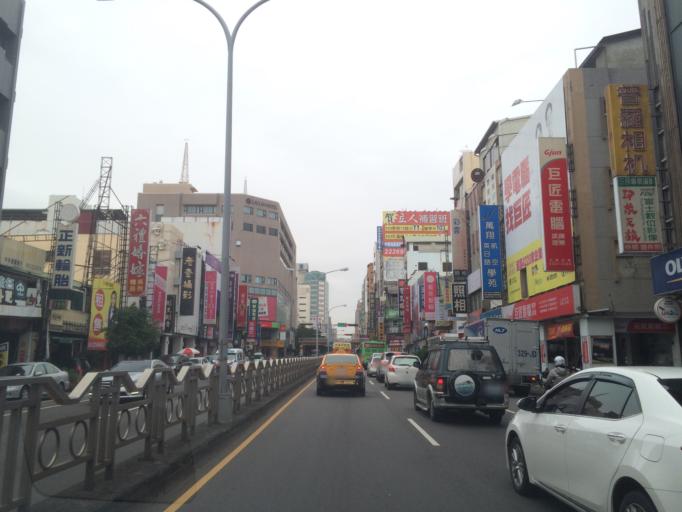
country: TW
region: Taiwan
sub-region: Taichung City
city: Taichung
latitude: 24.1473
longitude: 120.6831
